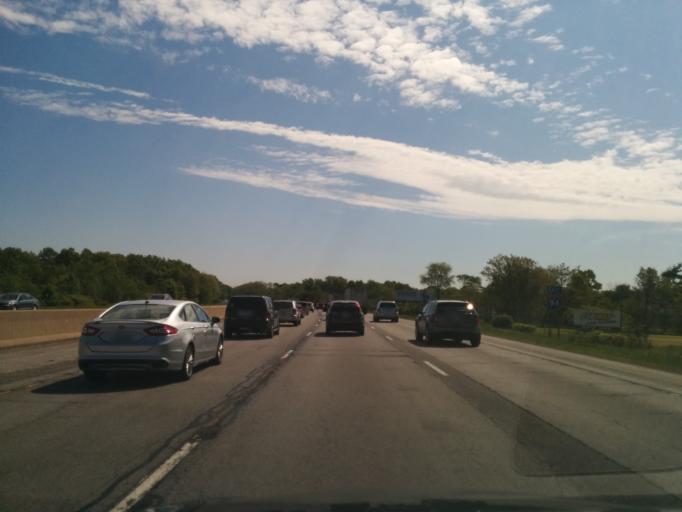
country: US
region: Indiana
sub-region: Porter County
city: Porter
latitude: 41.6076
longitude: -87.0990
